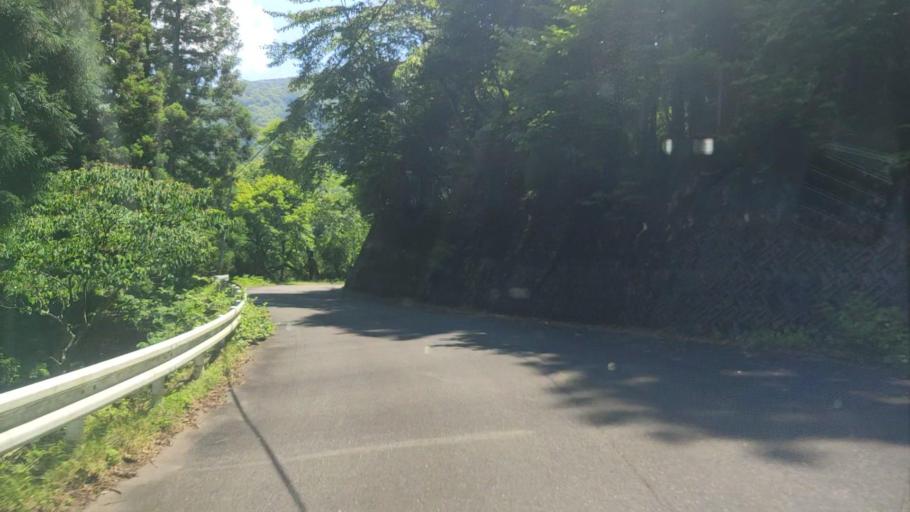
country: JP
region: Fukui
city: Ono
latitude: 35.7147
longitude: 136.5841
